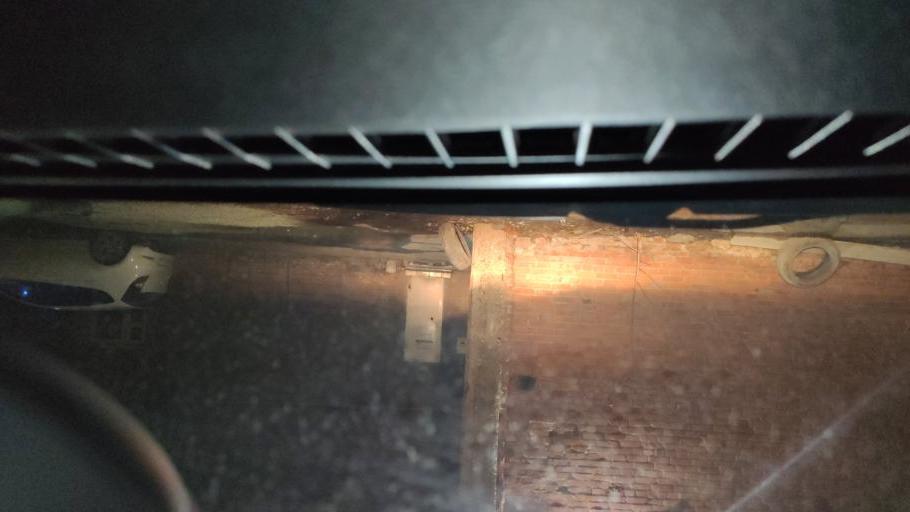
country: RU
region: Perm
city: Kondratovo
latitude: 57.9699
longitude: 56.1834
